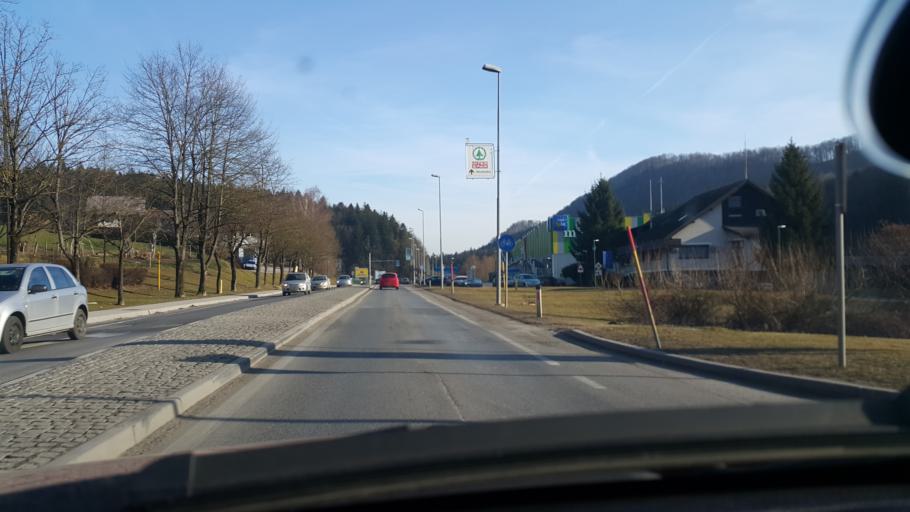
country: SI
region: Velenje
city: Velenje
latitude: 46.3563
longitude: 15.1150
